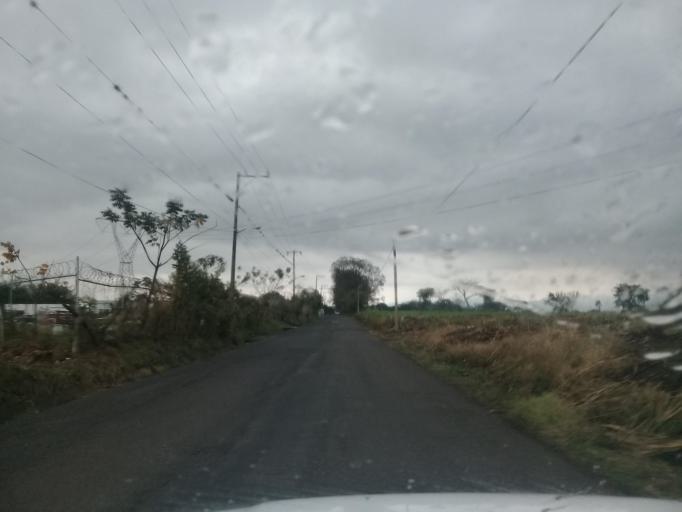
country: MX
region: Veracruz
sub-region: Cordoba
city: San Jose de Tapia
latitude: 18.8551
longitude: -96.9509
